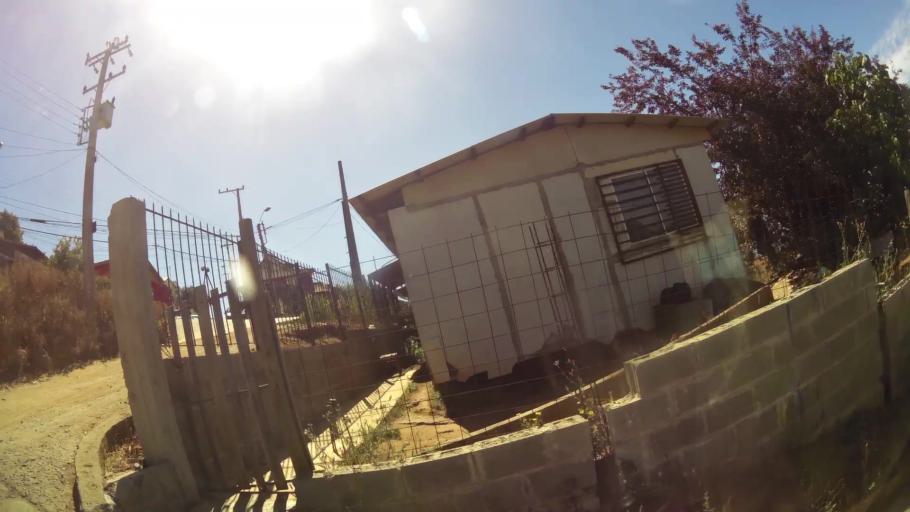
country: CL
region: Valparaiso
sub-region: Provincia de Valparaiso
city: Vina del Mar
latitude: -33.0419
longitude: -71.5658
